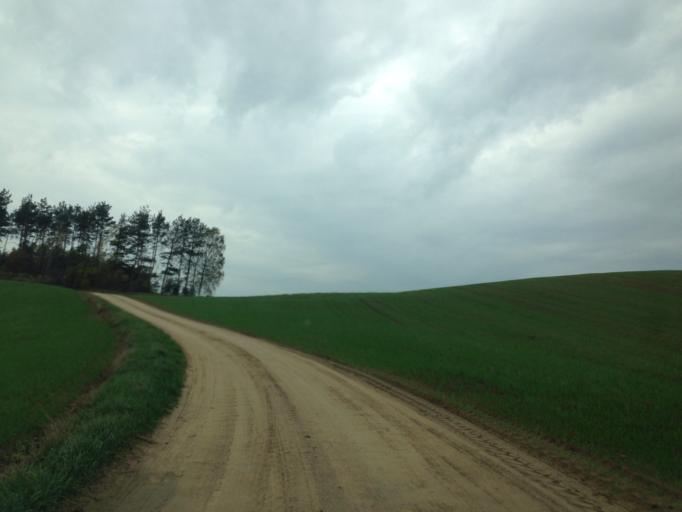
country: PL
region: Kujawsko-Pomorskie
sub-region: Powiat brodnicki
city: Bartniczka
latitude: 53.2698
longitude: 19.6632
